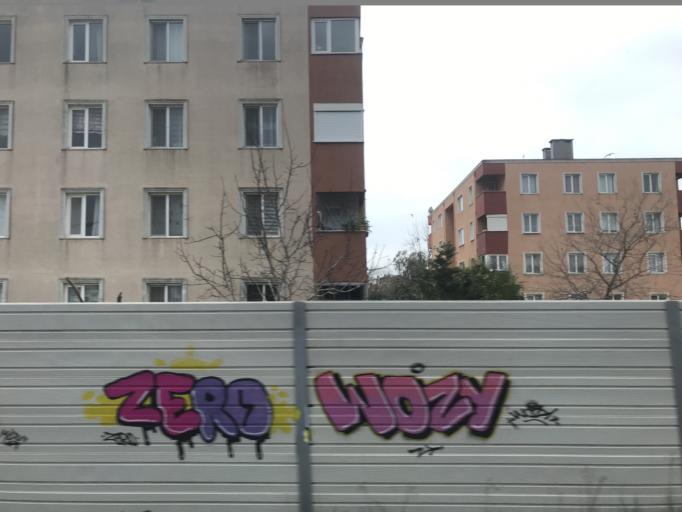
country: TR
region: Istanbul
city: Icmeler
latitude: 40.8424
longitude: 29.3043
